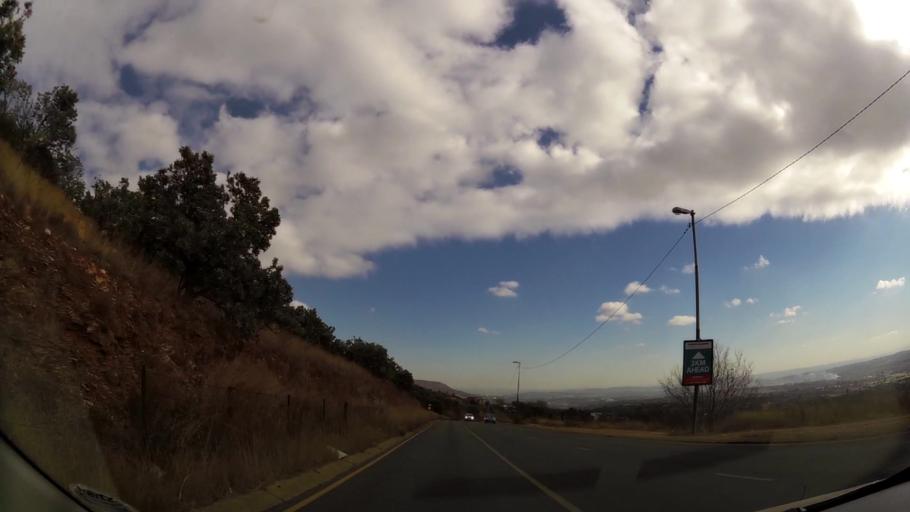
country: ZA
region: Gauteng
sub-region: City of Johannesburg Metropolitan Municipality
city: Roodepoort
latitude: -26.1032
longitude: 27.8653
